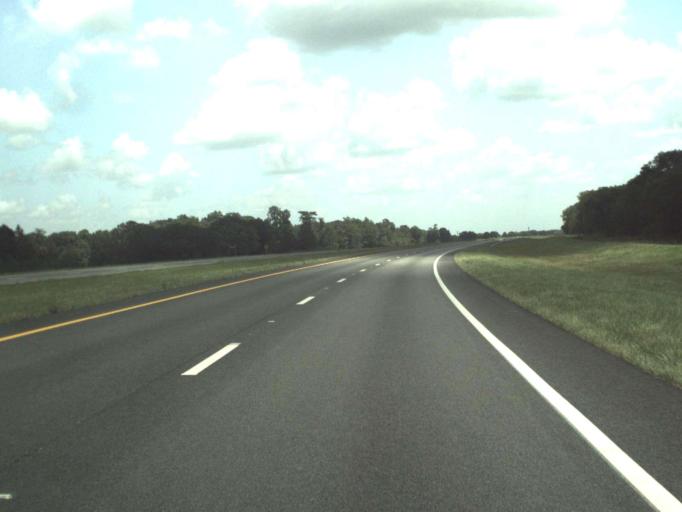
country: US
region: Florida
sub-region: Okeechobee County
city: Taylor Creek
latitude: 27.3281
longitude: -80.6526
